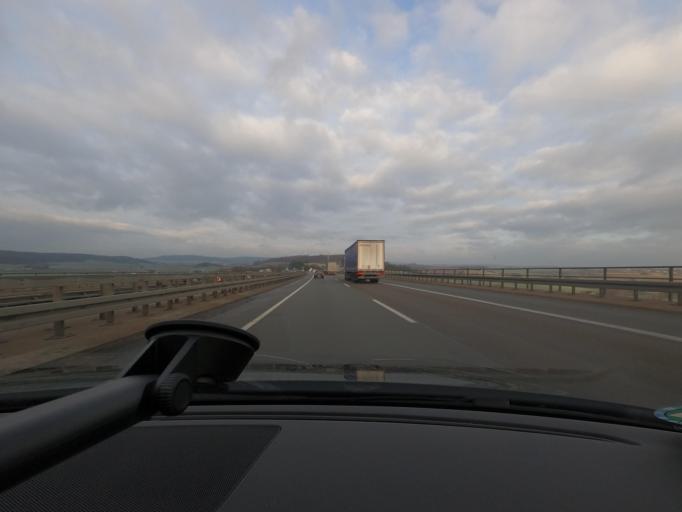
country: DE
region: North Rhine-Westphalia
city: Warburg
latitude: 51.4642
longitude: 9.1185
